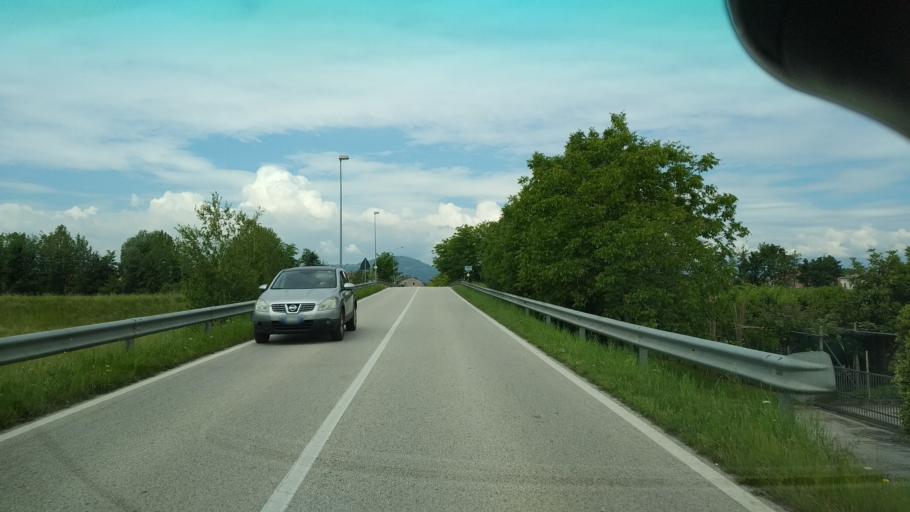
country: IT
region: Veneto
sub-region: Provincia di Vicenza
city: Monticello Conte Otto
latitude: 45.6003
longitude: 11.5378
